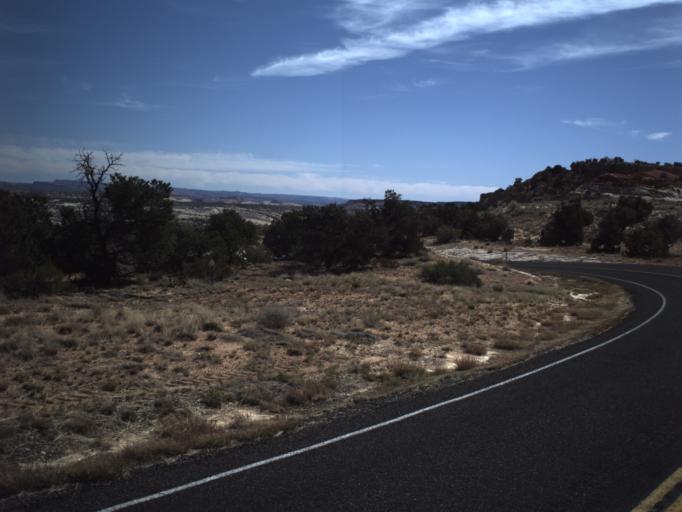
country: US
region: Utah
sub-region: Wayne County
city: Loa
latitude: 37.7422
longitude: -111.4541
